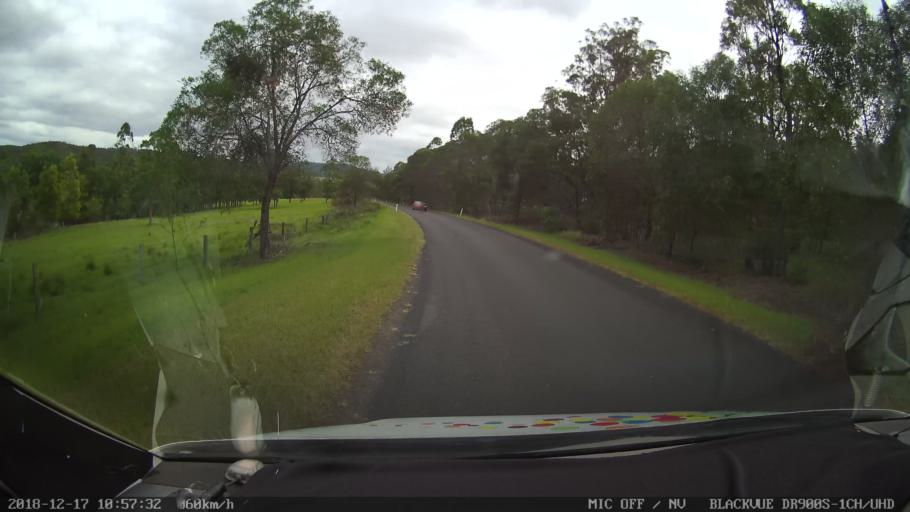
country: AU
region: New South Wales
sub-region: Richmond Valley
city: Casino
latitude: -28.8248
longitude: 152.5979
